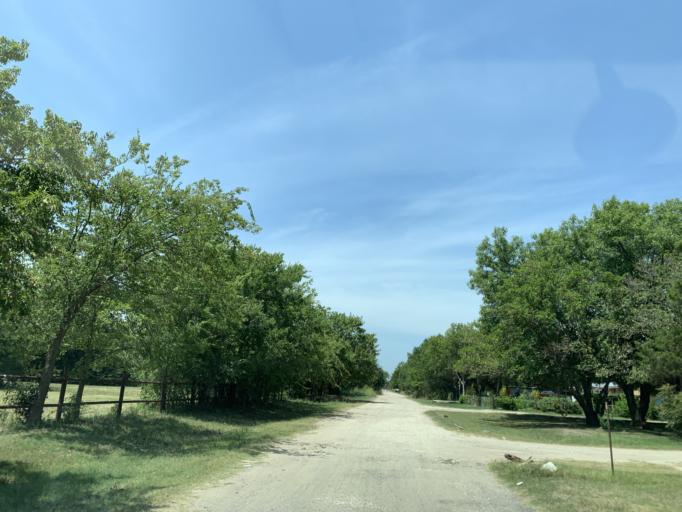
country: US
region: Texas
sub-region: Dallas County
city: Cedar Hill
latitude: 32.6411
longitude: -97.0235
